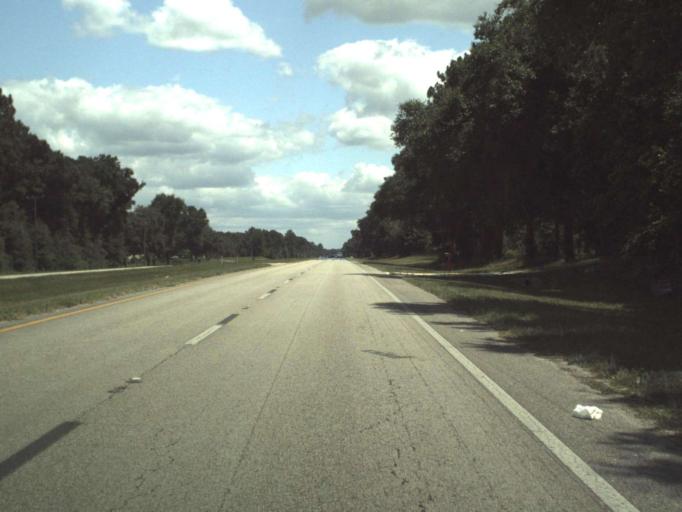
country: US
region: Florida
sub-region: Marion County
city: Citra
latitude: 29.3732
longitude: -82.1742
